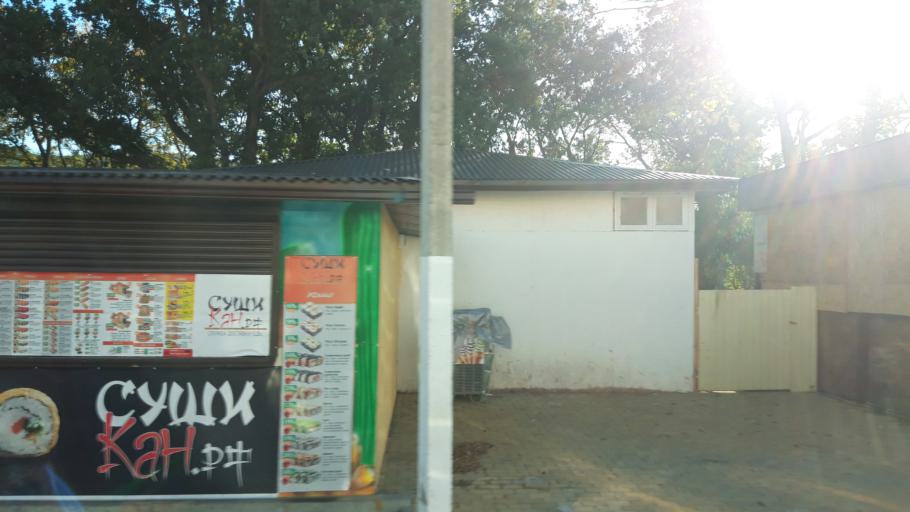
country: RU
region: Krasnodarskiy
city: Kabardinka
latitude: 44.6472
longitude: 37.9386
